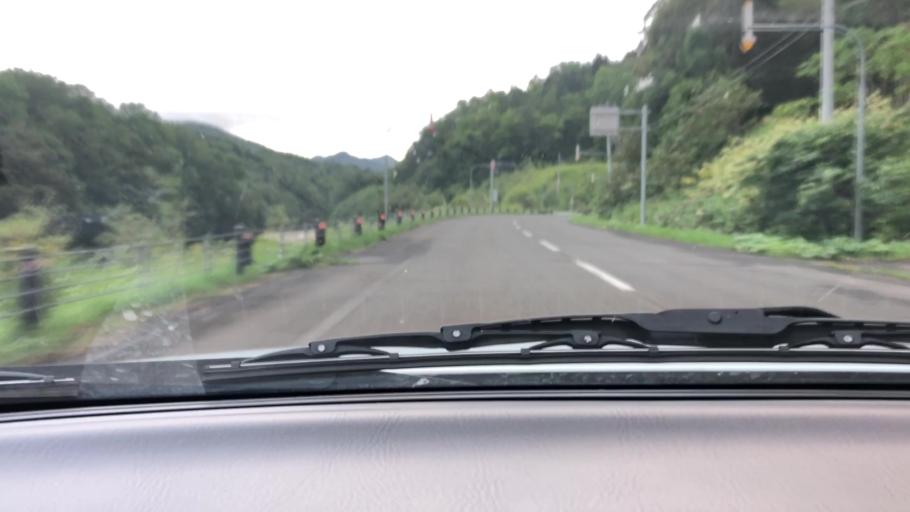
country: JP
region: Hokkaido
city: Shimo-furano
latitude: 42.9636
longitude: 142.3754
